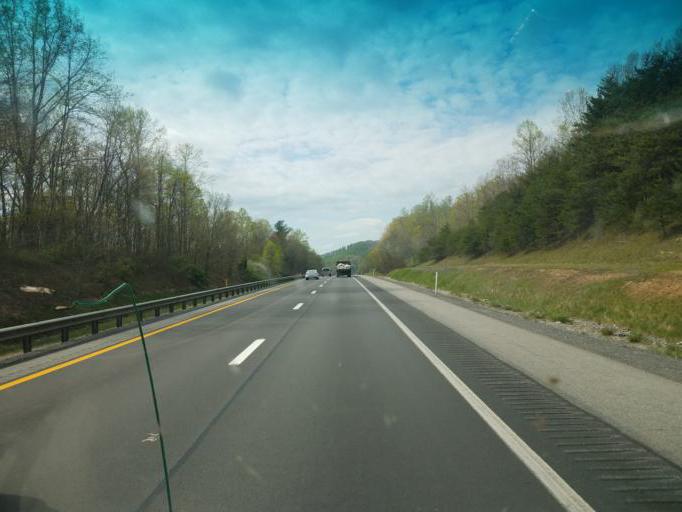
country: US
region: West Virginia
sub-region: Raleigh County
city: Bradley
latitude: 37.8908
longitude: -81.2671
